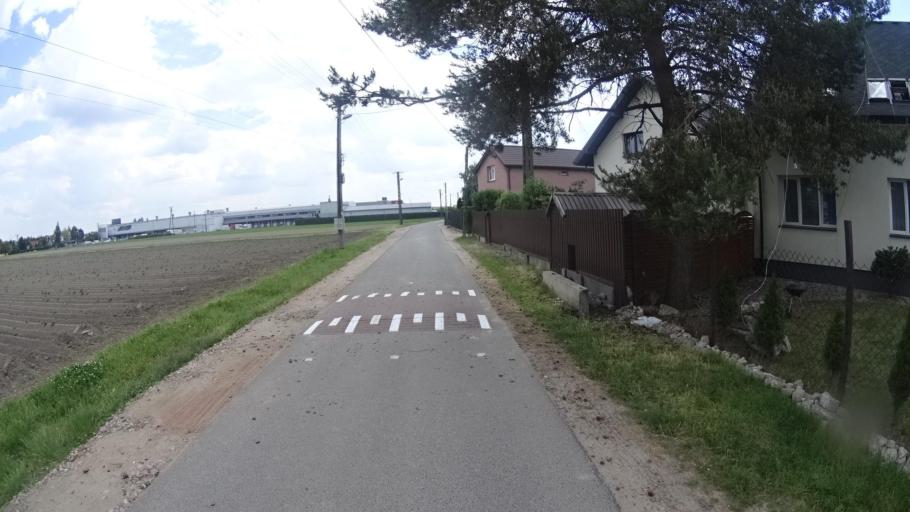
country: PL
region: Masovian Voivodeship
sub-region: Powiat pruszkowski
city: Piastow
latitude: 52.2115
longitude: 20.8354
